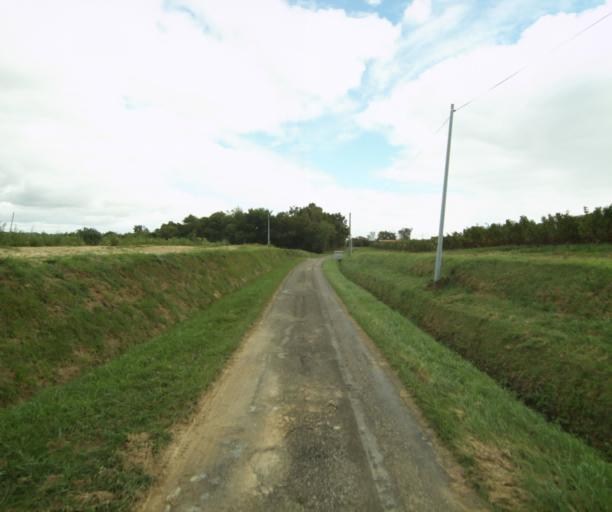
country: FR
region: Midi-Pyrenees
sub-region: Departement du Gers
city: Cazaubon
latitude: 43.8637
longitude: -0.0258
